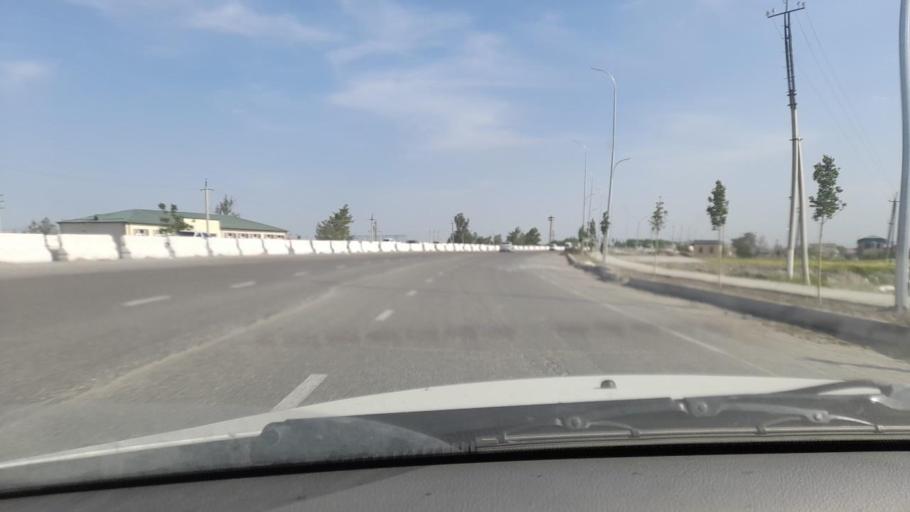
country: UZ
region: Samarqand
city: Daxbet
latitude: 39.7267
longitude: 66.9462
